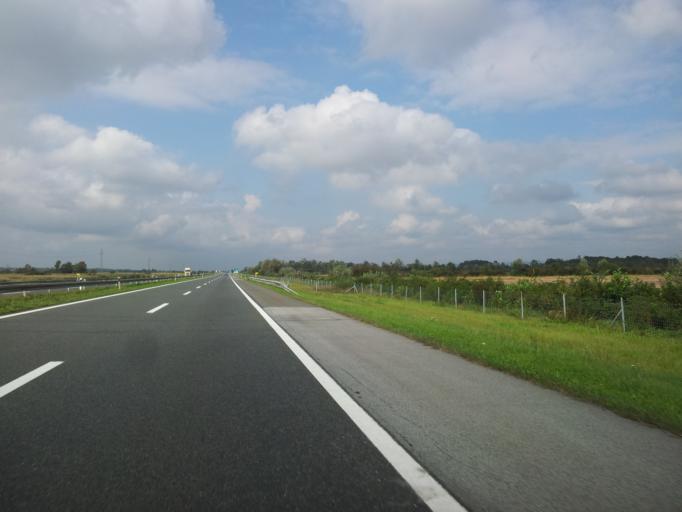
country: HR
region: Brodsko-Posavska
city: Ljupina
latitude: 45.2284
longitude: 17.3293
